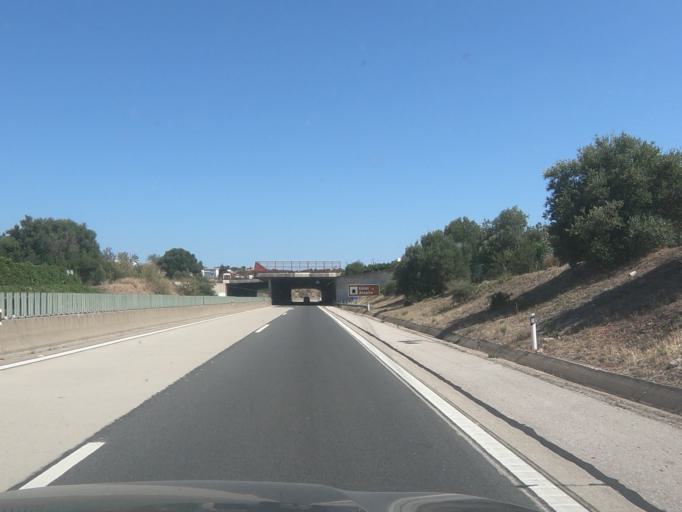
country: PT
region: Faro
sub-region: Loule
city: Loule
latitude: 37.1133
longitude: -8.0234
